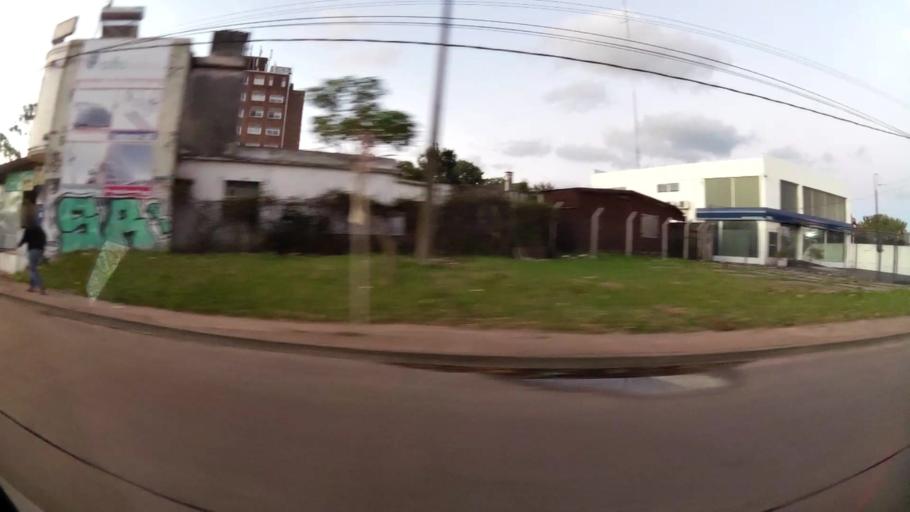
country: UY
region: Canelones
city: Paso de Carrasco
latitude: -34.8858
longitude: -56.1005
